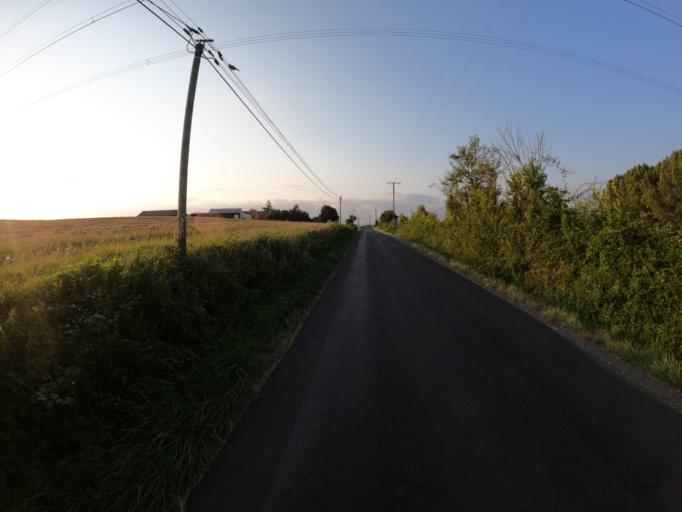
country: FR
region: Pays de la Loire
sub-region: Departement de la Sarthe
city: Parce-sur-Sarthe
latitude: 47.8734
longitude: -0.2059
